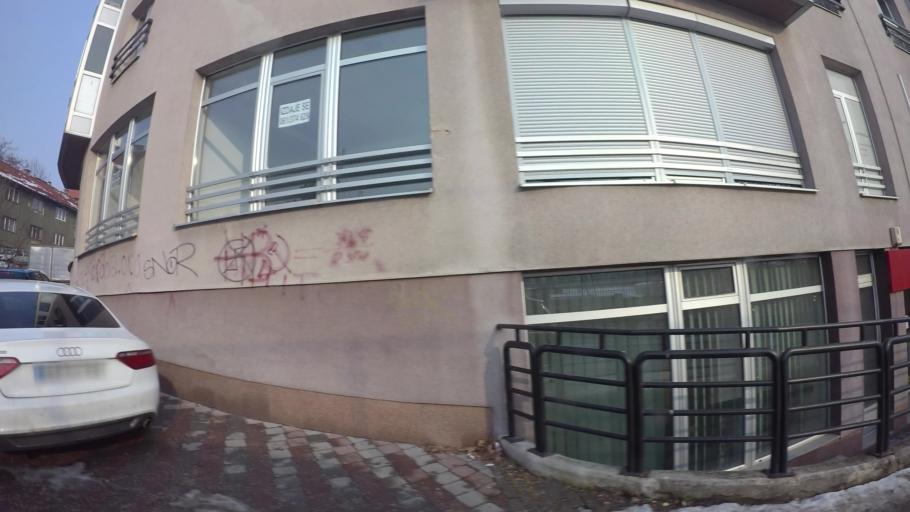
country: BA
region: Federation of Bosnia and Herzegovina
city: Kobilja Glava
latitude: 43.8659
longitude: 18.4006
